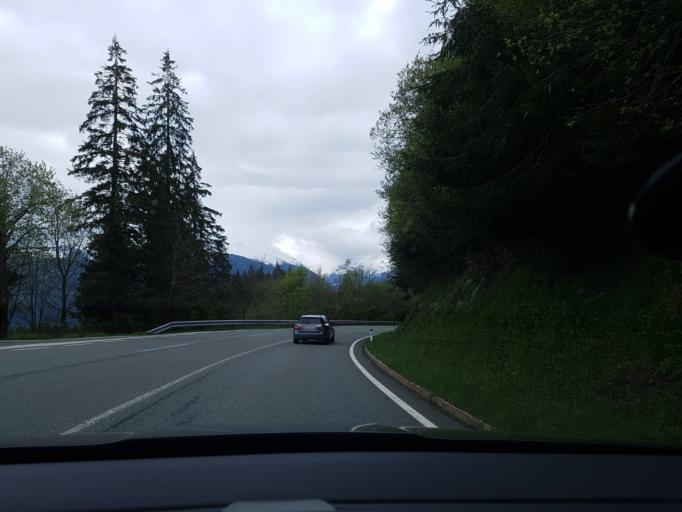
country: AT
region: Salzburg
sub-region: Politischer Bezirk Zell am See
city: Hollersbach im Pinzgau
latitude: 47.3049
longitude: 12.4114
